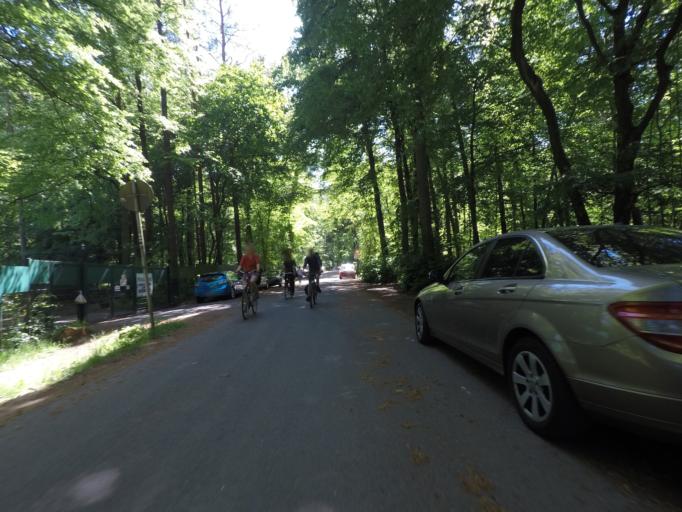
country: DE
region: Brandenburg
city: Eberswalde
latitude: 52.8229
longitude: 13.7796
